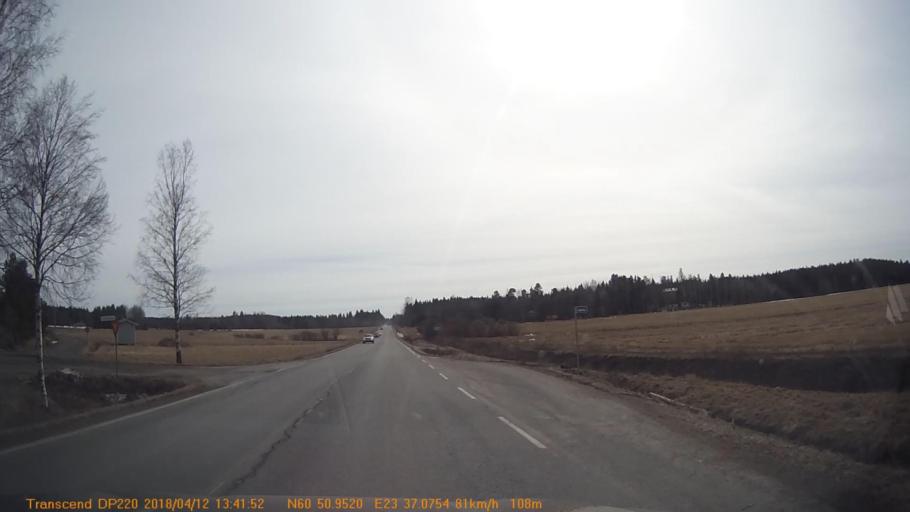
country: FI
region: Haeme
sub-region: Forssa
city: Forssa
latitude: 60.8485
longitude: 23.6179
